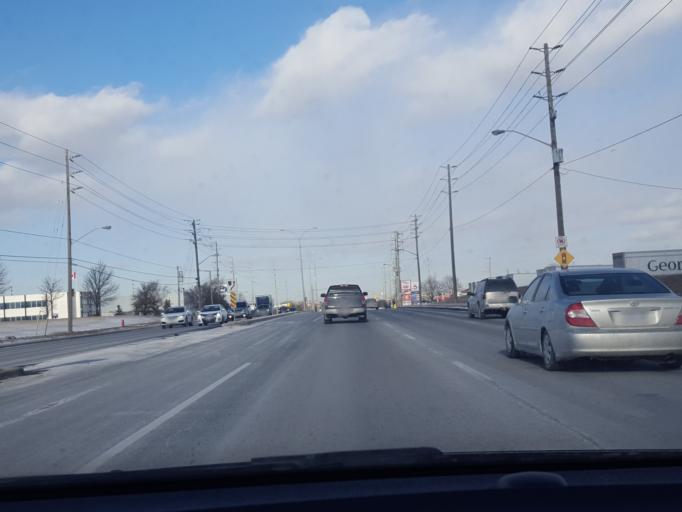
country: CA
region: Ontario
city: Brampton
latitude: 43.6928
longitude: -79.7037
